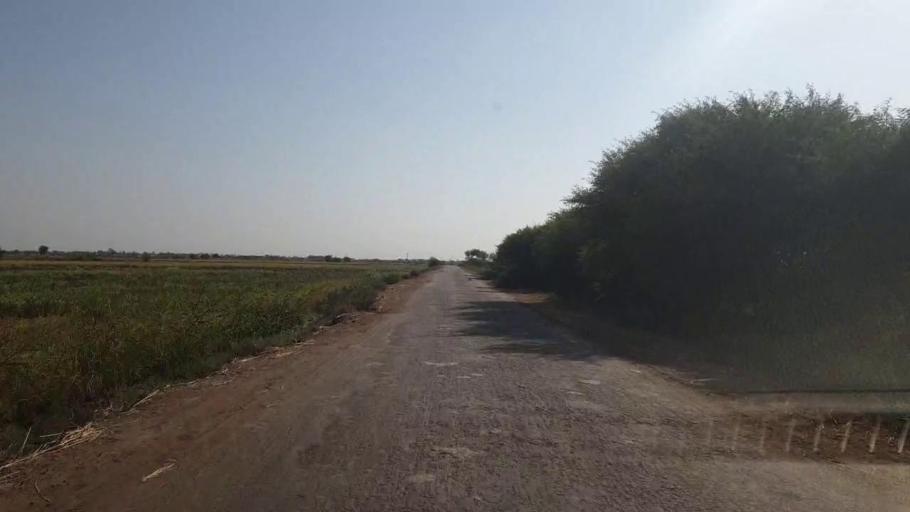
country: PK
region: Sindh
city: Matli
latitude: 25.0480
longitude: 68.7235
